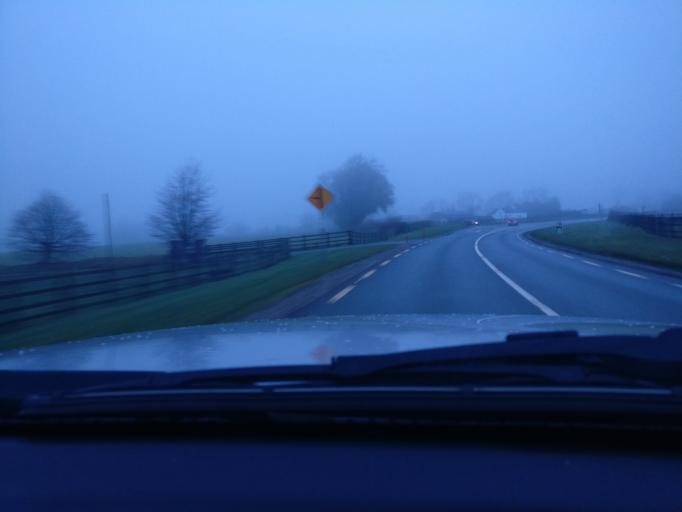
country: IE
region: Leinster
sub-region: An Mhi
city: Athboy
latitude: 53.6368
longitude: -6.8939
